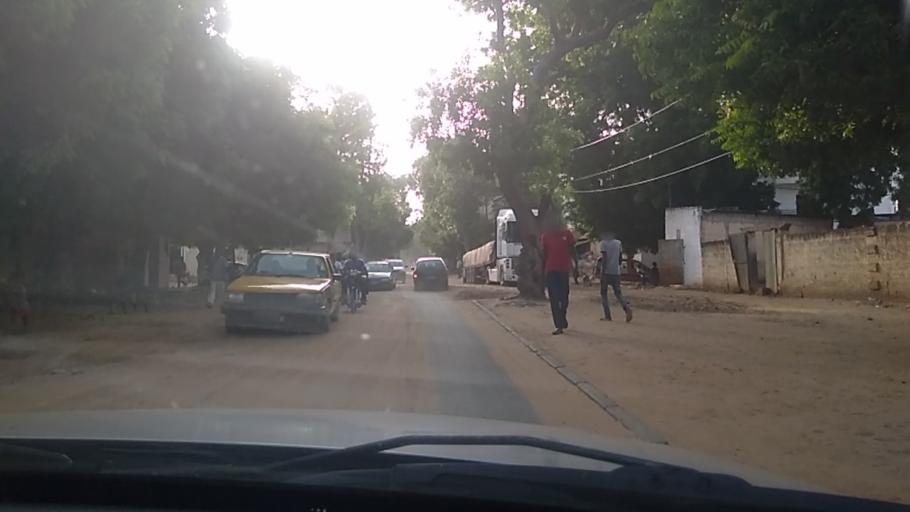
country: SN
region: Thies
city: Thies Nones
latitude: 14.7860
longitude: -16.9268
